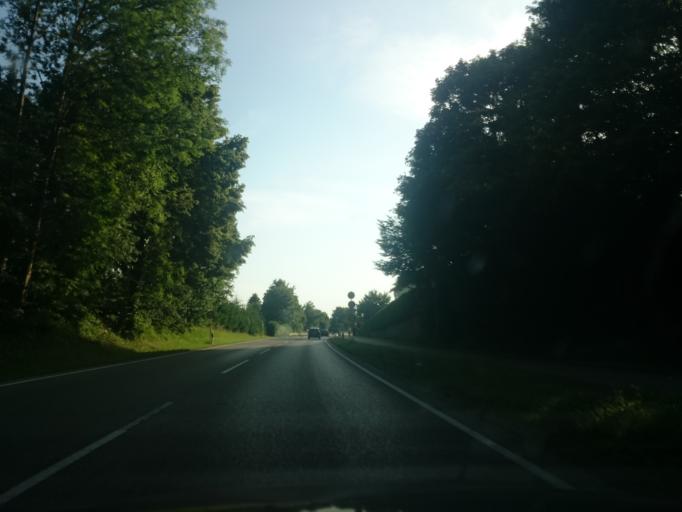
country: DE
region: Bavaria
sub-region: Upper Bavaria
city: Gilching
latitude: 48.1097
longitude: 11.3282
